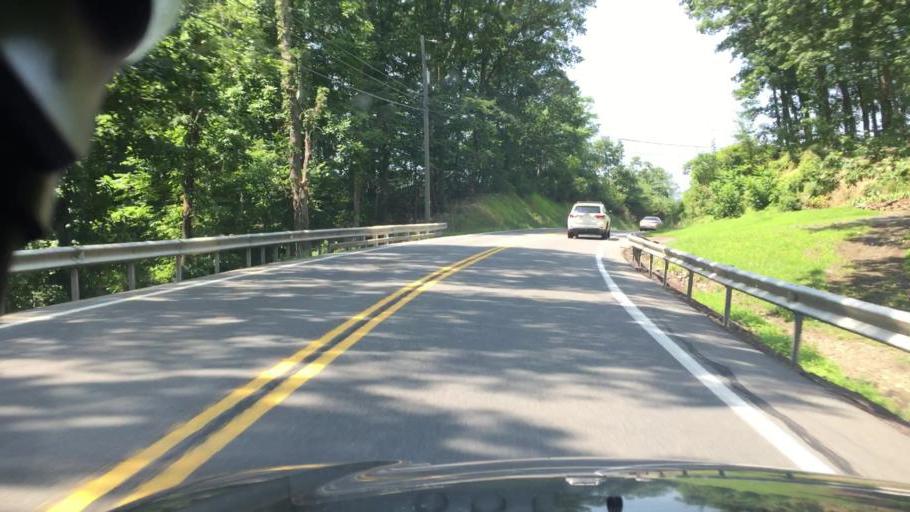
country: US
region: Pennsylvania
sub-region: Columbia County
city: Catawissa
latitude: 40.9019
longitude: -76.4853
